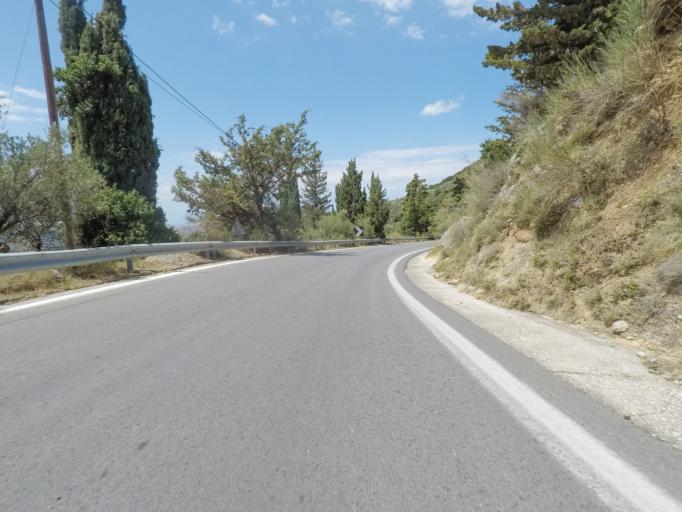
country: GR
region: Crete
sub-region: Nomos Irakleiou
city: Mokhos
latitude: 35.2233
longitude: 25.4620
